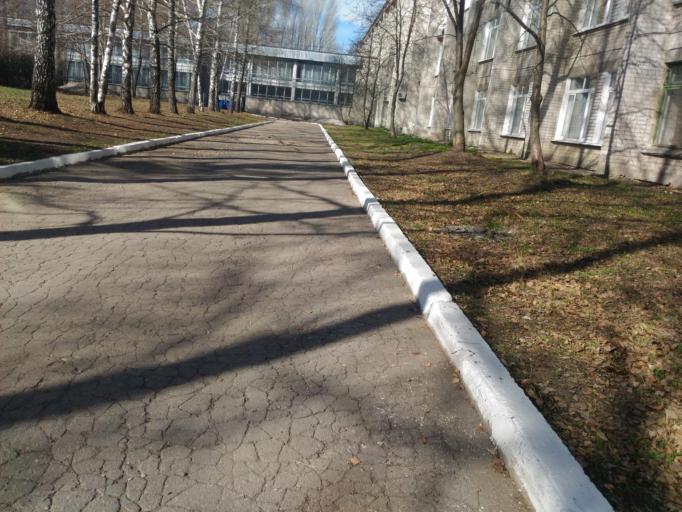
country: RU
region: Ulyanovsk
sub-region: Ulyanovskiy Rayon
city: Ulyanovsk
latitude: 54.3529
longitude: 48.3889
